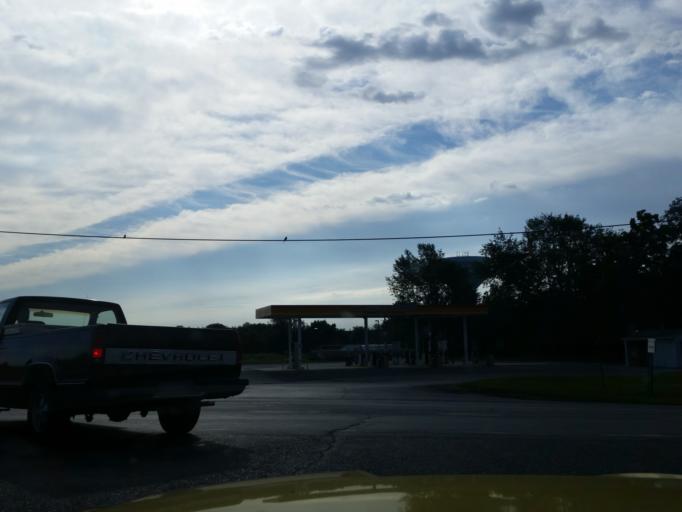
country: US
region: Pennsylvania
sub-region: Lebanon County
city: Fredericksburg
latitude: 40.4503
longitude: -76.4161
